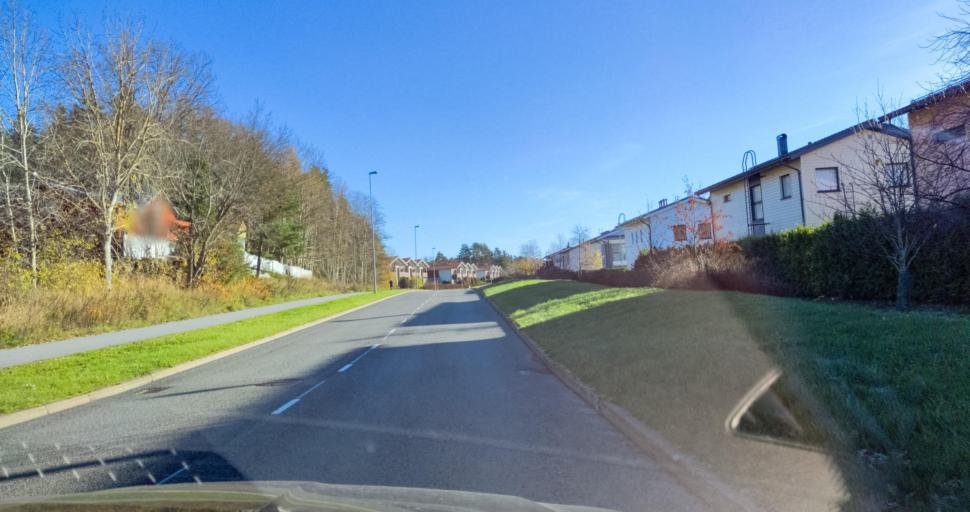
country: FI
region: Varsinais-Suomi
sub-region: Turku
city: Turku
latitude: 60.4108
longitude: 22.2120
